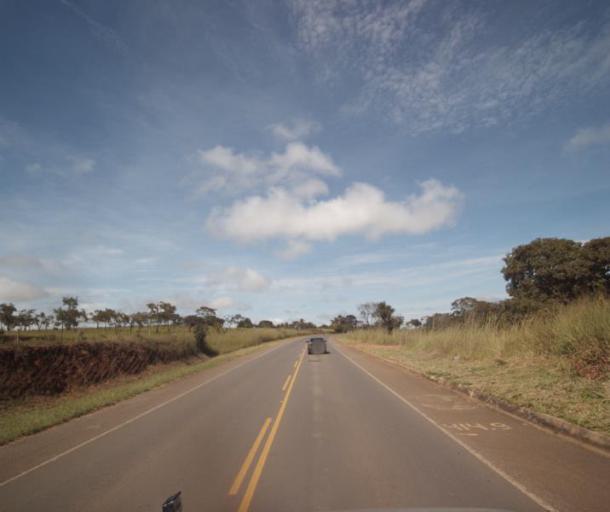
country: BR
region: Goias
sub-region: Abadiania
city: Abadiania
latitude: -16.0974
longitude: -48.8548
